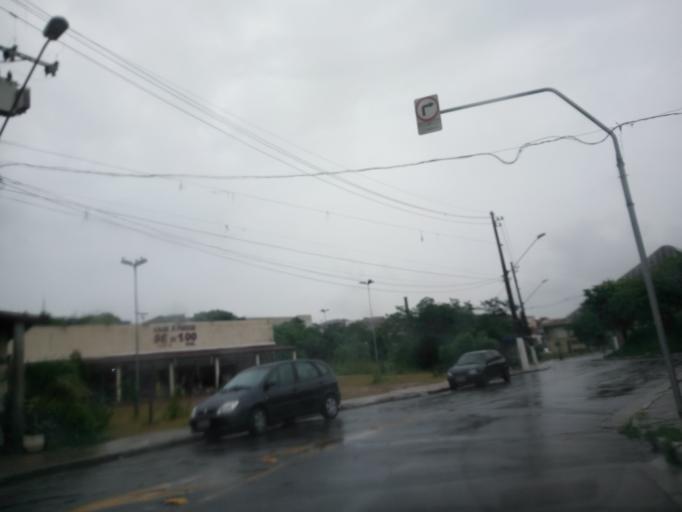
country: BR
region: Sao Paulo
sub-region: Sao Bernardo Do Campo
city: Sao Bernardo do Campo
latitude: -23.7227
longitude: -46.5921
